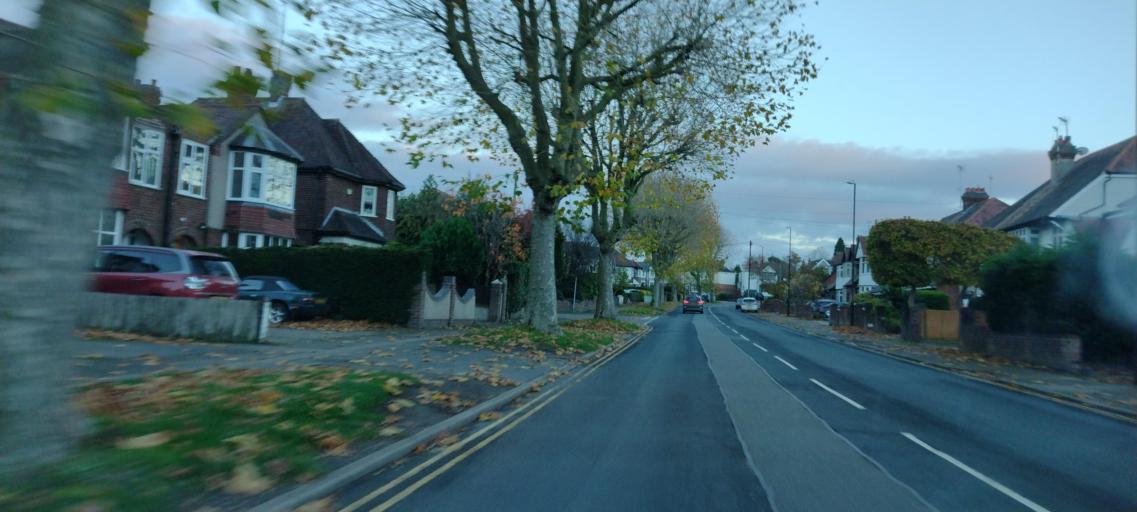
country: GB
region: England
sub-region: Coventry
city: Coventry
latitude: 52.4000
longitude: -1.5397
